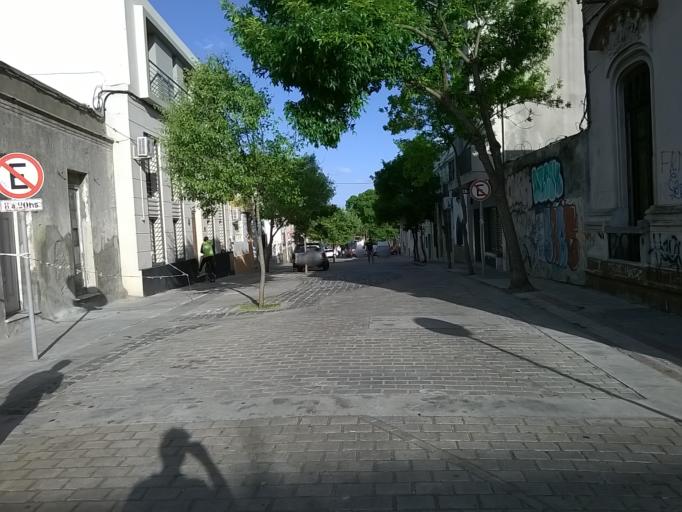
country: UY
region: Montevideo
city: Montevideo
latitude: -34.9094
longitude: -56.1804
